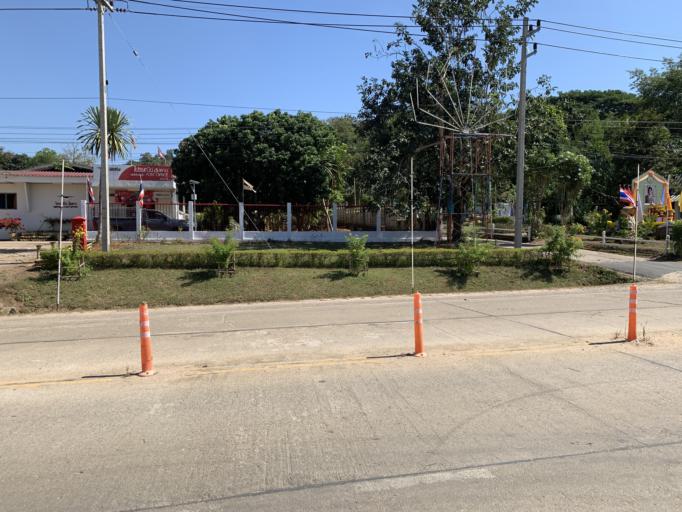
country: TH
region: Tak
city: Umphang
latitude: 16.0247
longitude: 98.8595
